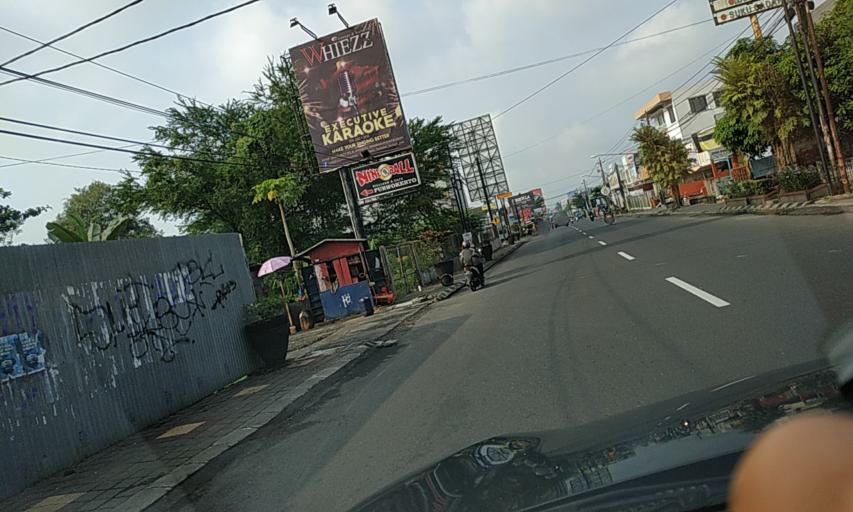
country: ID
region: Central Java
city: Purwokerto
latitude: -7.4193
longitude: 109.2444
